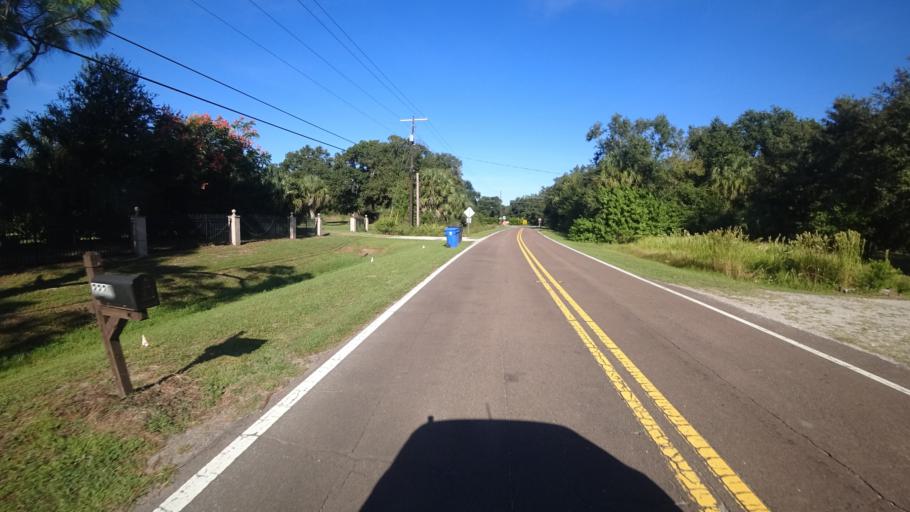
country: US
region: Florida
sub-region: Hillsborough County
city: Ruskin
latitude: 27.6490
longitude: -82.4206
